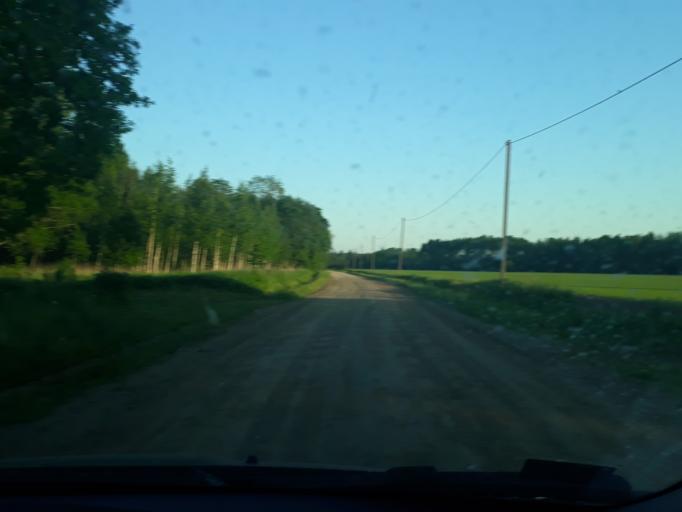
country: EE
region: Paernumaa
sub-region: Vaendra vald (alev)
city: Vandra
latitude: 58.5730
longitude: 24.9454
